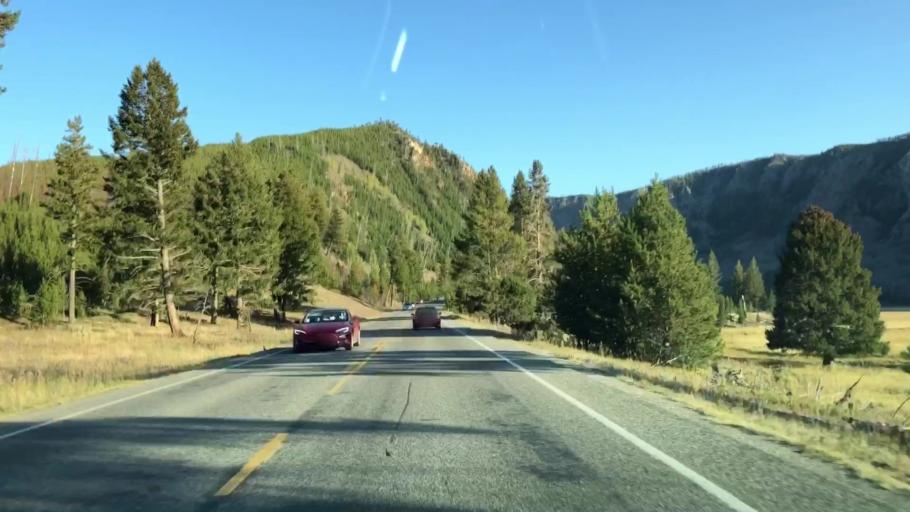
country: US
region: Montana
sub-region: Gallatin County
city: West Yellowstone
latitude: 44.6598
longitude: -110.9601
